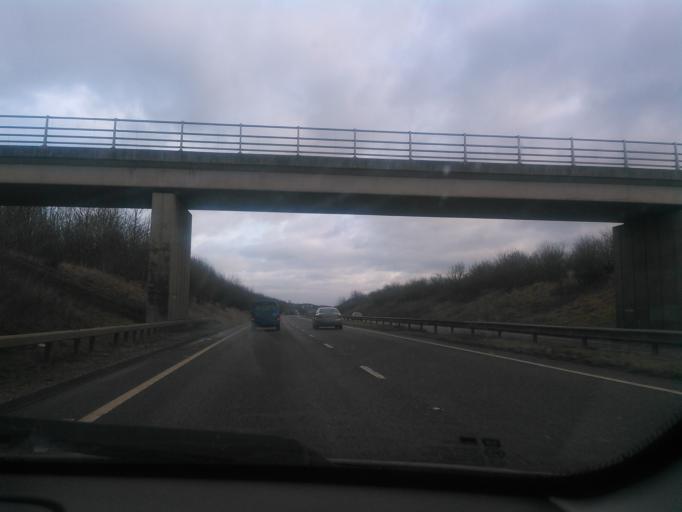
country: GB
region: England
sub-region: Derbyshire
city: Melbourne
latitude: 52.8630
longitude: -1.4601
